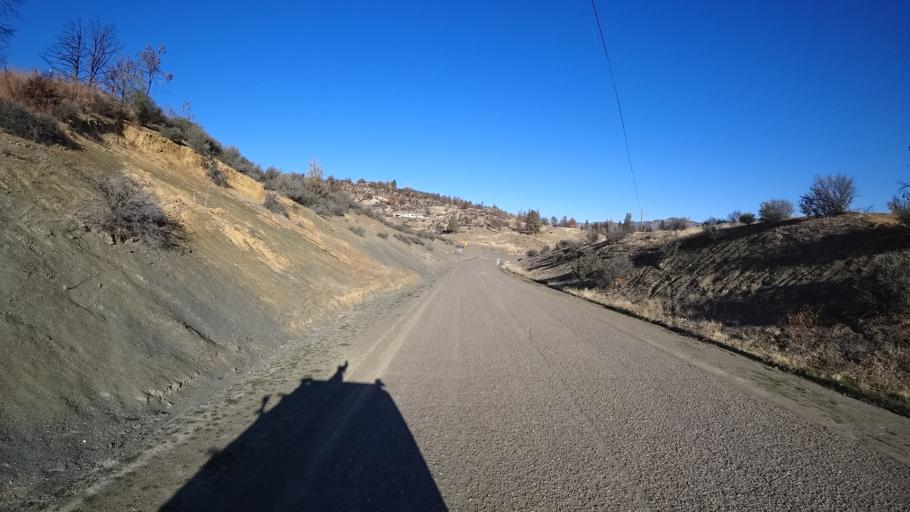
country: US
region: California
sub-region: Siskiyou County
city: Montague
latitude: 41.8999
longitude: -122.5681
